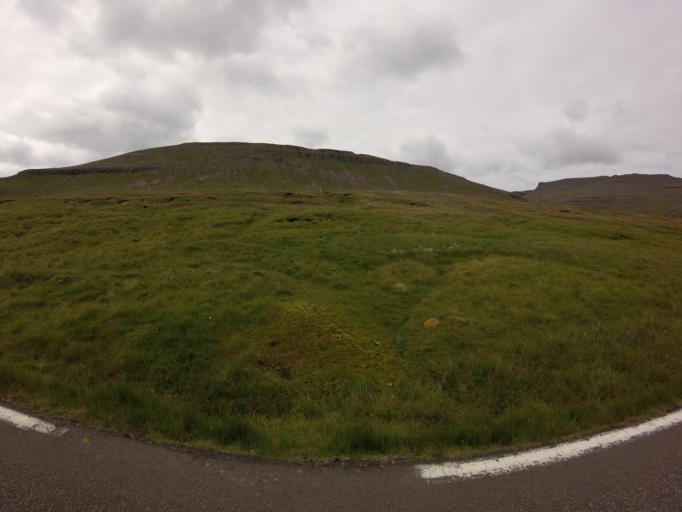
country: FO
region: Suduroy
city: Tvoroyri
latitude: 61.5338
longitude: -6.8349
